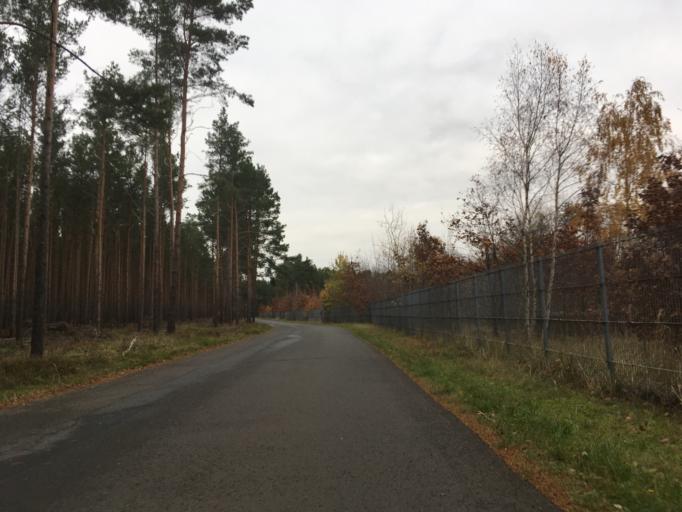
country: DE
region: Brandenburg
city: Mullrose
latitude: 52.2677
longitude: 14.4784
